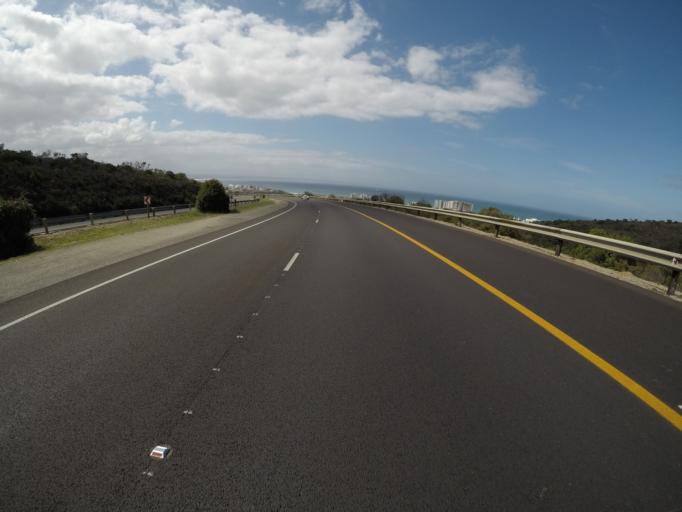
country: ZA
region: Western Cape
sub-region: Eden District Municipality
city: Mossel Bay
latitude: -34.1605
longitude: 22.0978
